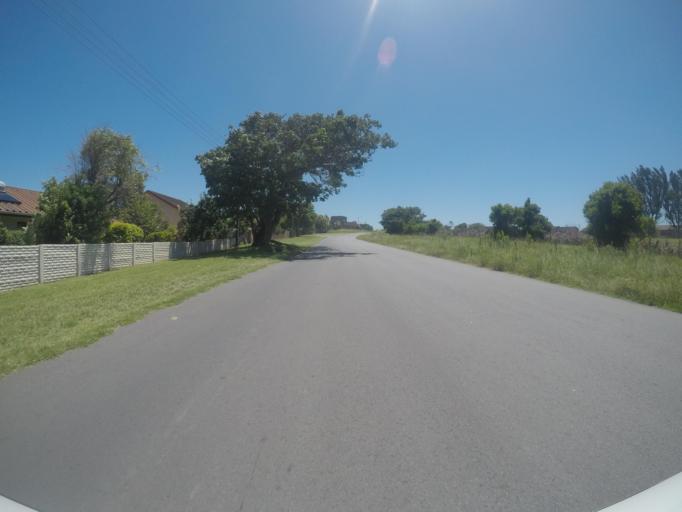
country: ZA
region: Eastern Cape
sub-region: Buffalo City Metropolitan Municipality
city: East London
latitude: -32.9541
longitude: 28.0002
